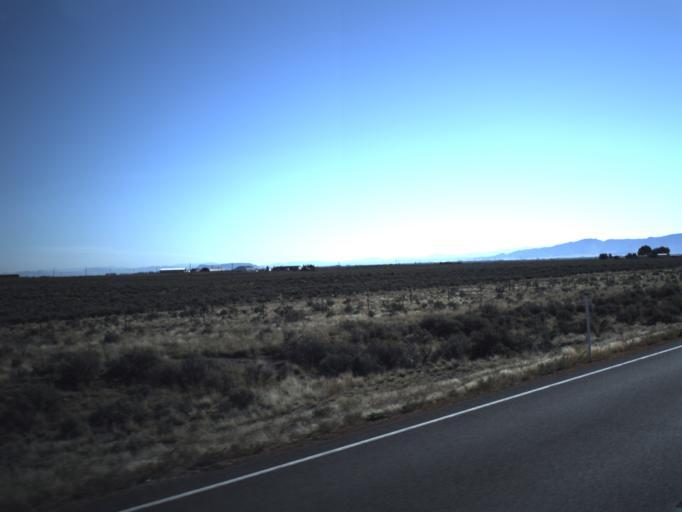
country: US
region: Utah
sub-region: Washington County
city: Enterprise
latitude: 37.7610
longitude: -113.8018
